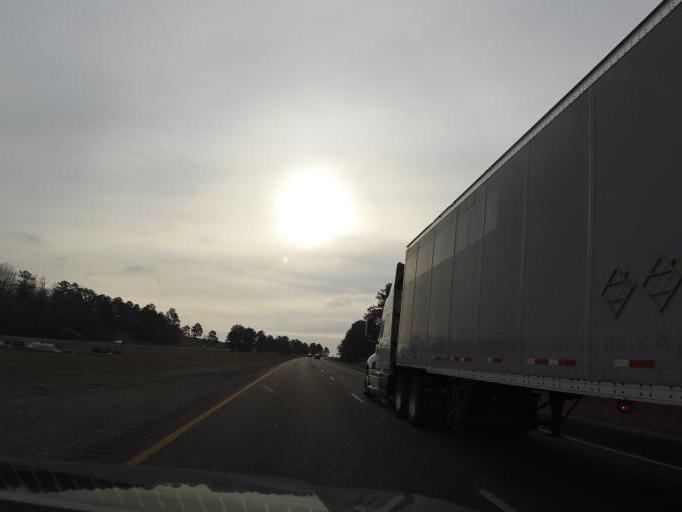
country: US
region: Alabama
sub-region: Autauga County
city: Prattville
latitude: 32.5134
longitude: -86.4294
